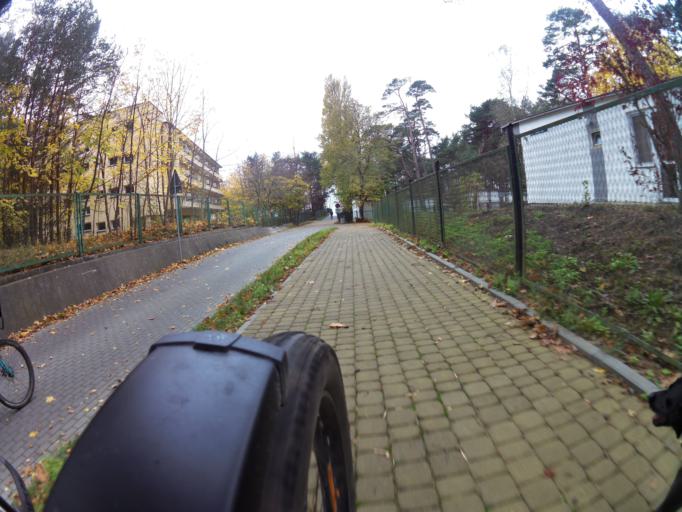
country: PL
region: Pomeranian Voivodeship
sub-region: Powiat pucki
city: Jastarnia
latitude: 54.6754
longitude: 18.7218
